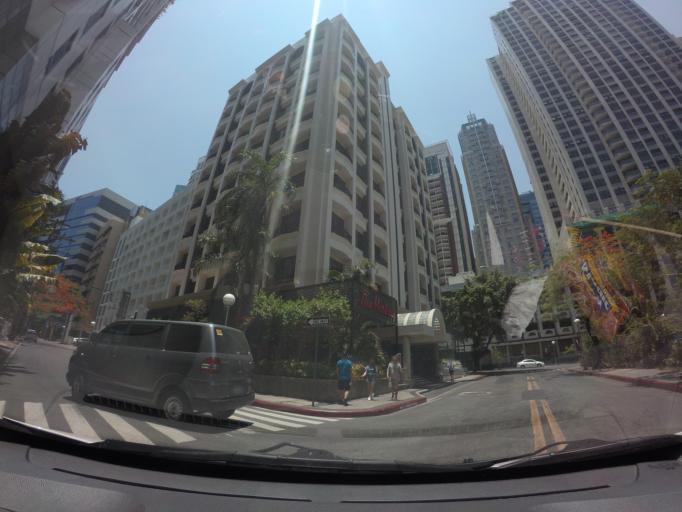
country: PH
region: Metro Manila
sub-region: Makati City
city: Makati City
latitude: 14.5603
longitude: 121.0235
